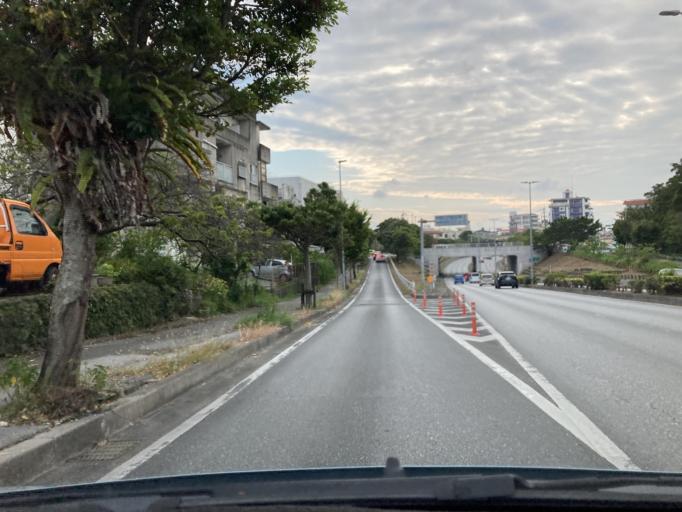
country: JP
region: Okinawa
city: Okinawa
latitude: 26.3389
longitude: 127.7966
